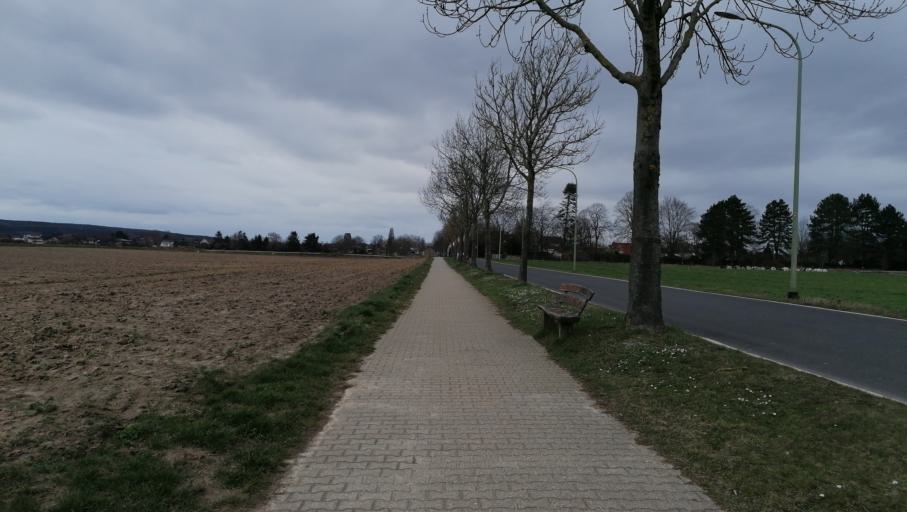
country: DE
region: North Rhine-Westphalia
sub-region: Regierungsbezirk Koln
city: Dueren
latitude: 50.7963
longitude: 6.4403
